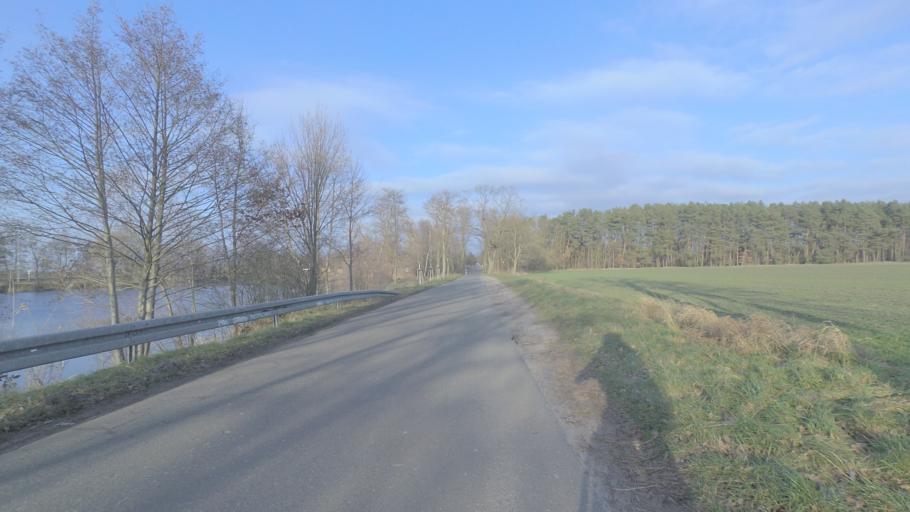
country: DE
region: Brandenburg
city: Rangsdorf
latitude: 52.2759
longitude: 13.4385
